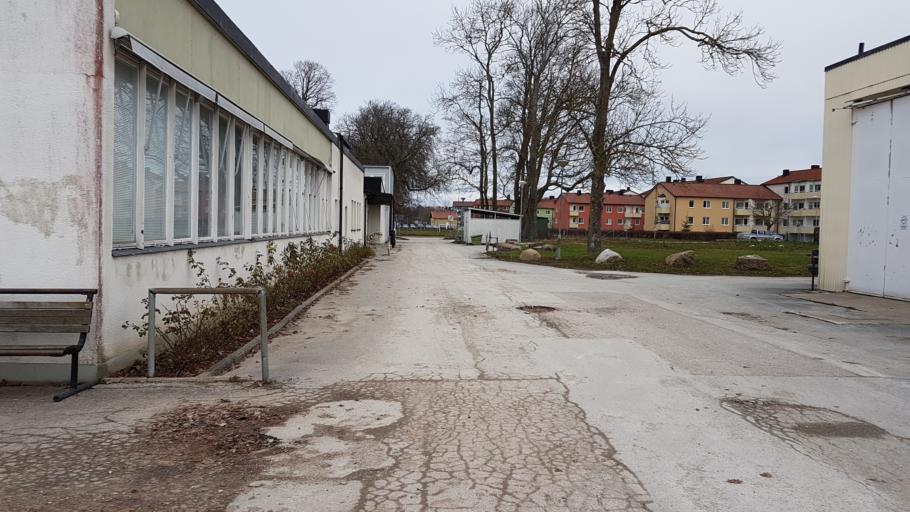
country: SE
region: Gotland
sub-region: Gotland
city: Visby
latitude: 57.6257
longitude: 18.2966
